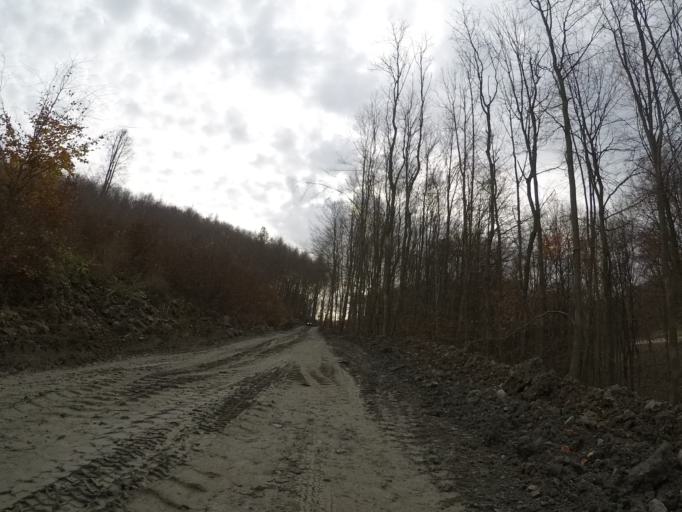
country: SK
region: Presovsky
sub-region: Okres Presov
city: Presov
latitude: 48.9774
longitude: 21.2160
